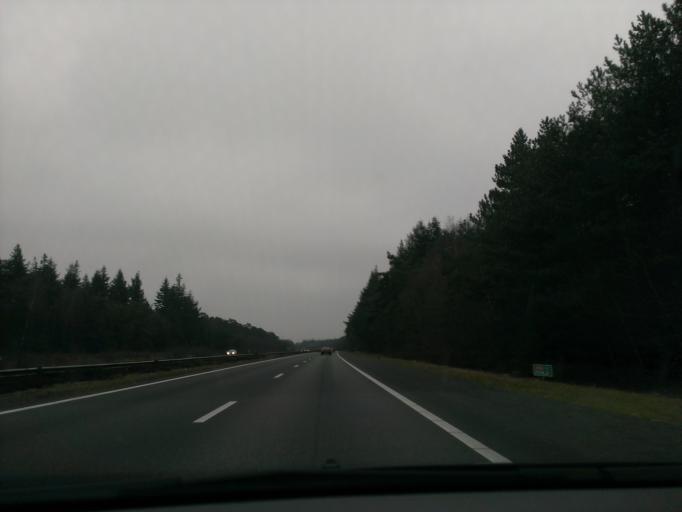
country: NL
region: Gelderland
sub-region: Gemeente Hattem
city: Hattem
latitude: 52.4519
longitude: 6.0293
